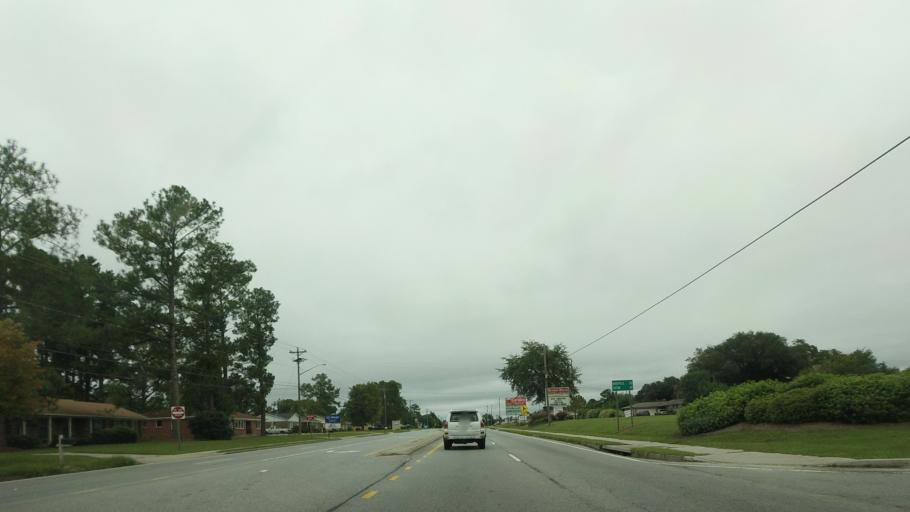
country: US
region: Georgia
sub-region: Lowndes County
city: Valdosta
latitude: 30.8844
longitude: -83.2728
